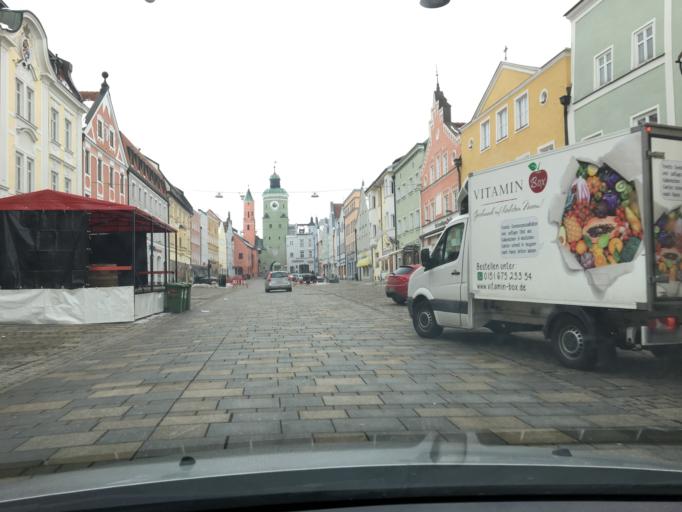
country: DE
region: Bavaria
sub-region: Lower Bavaria
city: Vilsbiburg
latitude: 48.4488
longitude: 12.3554
